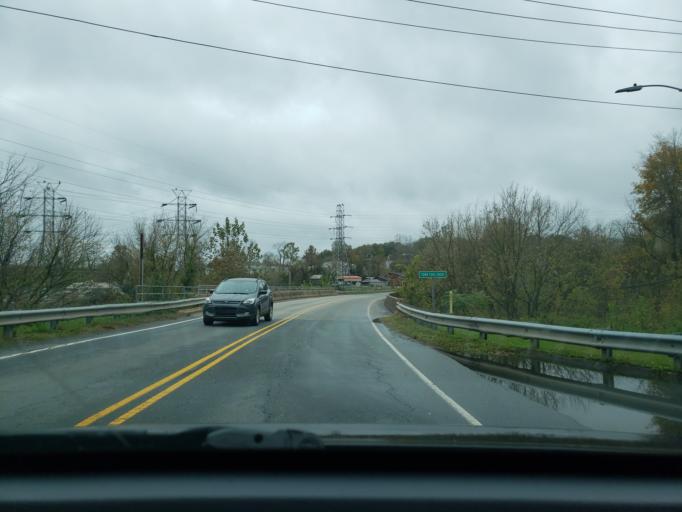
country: US
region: North Carolina
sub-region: Stokes County
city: Walnut Cove
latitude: 36.2922
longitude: -80.1411
